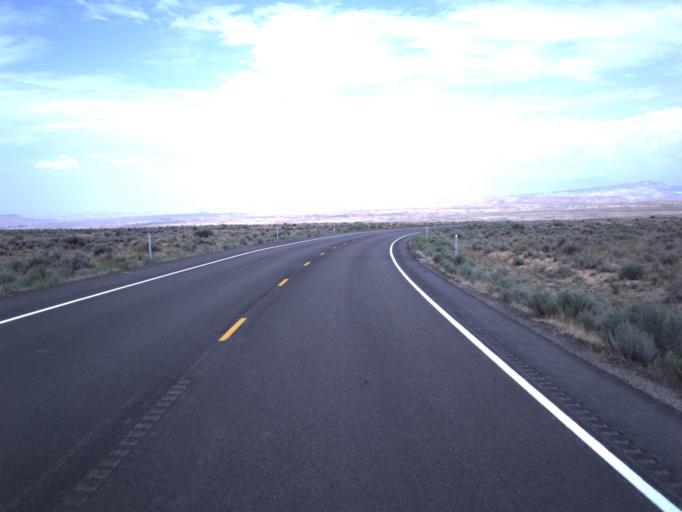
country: US
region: Utah
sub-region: Uintah County
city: Naples
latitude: 40.2292
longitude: -109.4078
